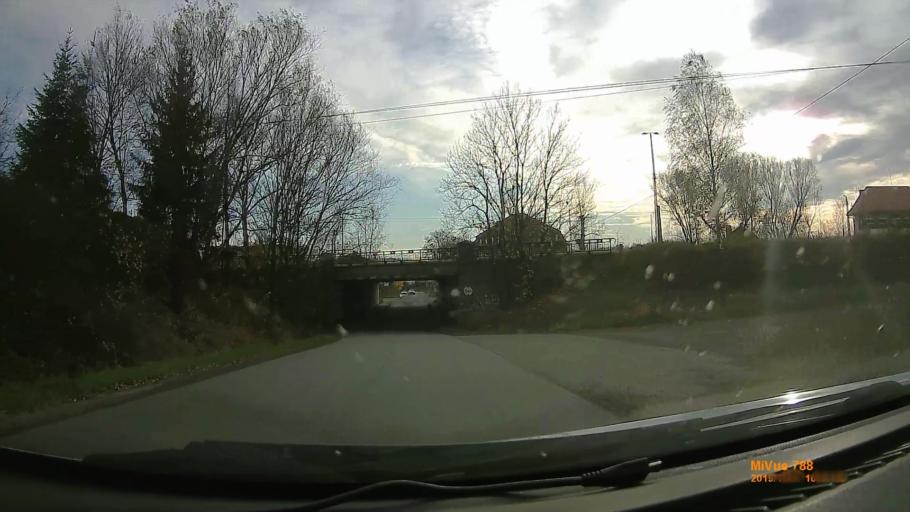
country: PL
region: Lower Silesian Voivodeship
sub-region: Powiat klodzki
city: Nowa Ruda
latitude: 50.5251
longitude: 16.5095
